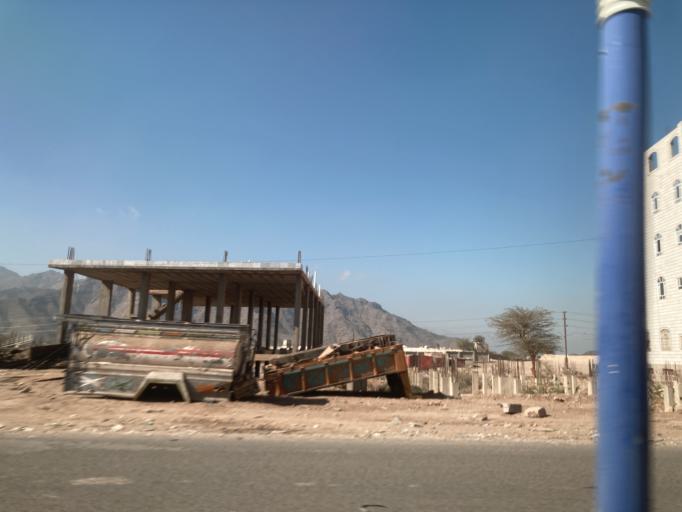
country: YE
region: Ad Dali'
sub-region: Qa'atabah
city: Qa`tabah
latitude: 13.8183
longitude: 44.7148
